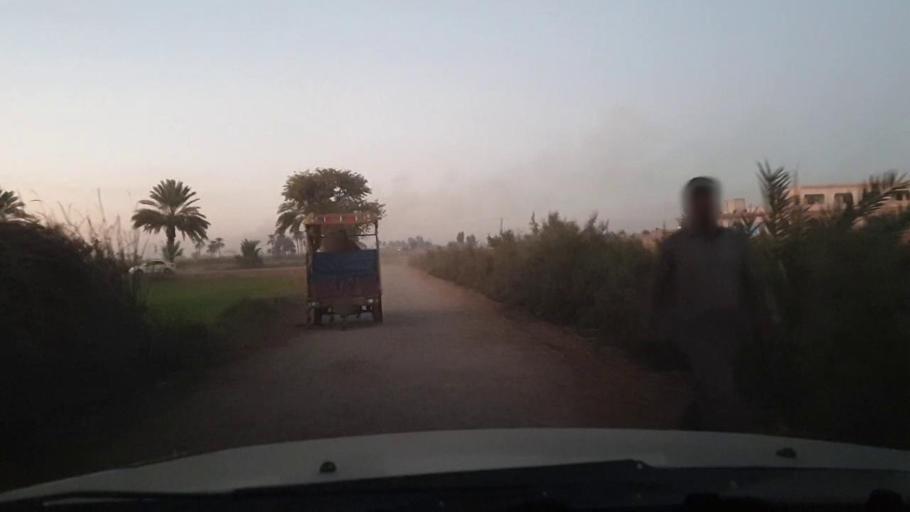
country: PK
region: Sindh
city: Ghotki
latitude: 27.9843
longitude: 69.2870
